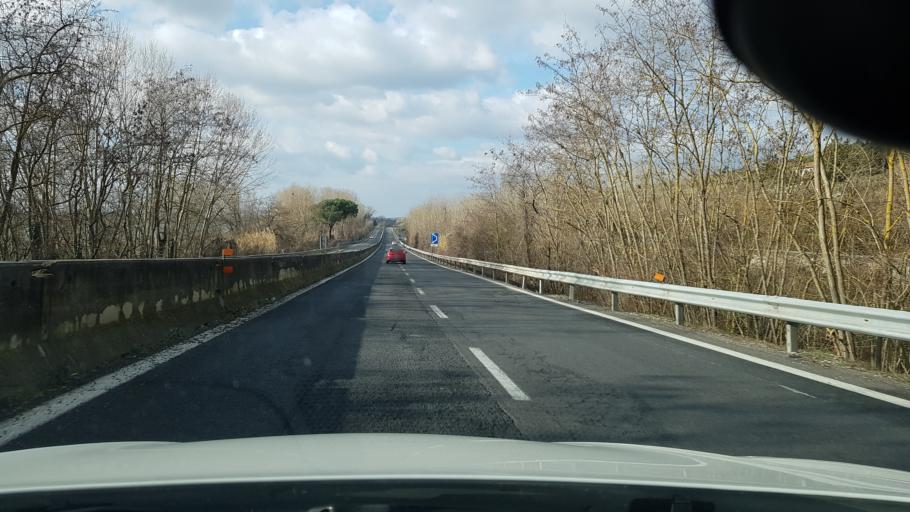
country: IT
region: Umbria
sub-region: Provincia di Perugia
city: Tuoro sul Trasimeno
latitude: 43.1890
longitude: 12.0471
